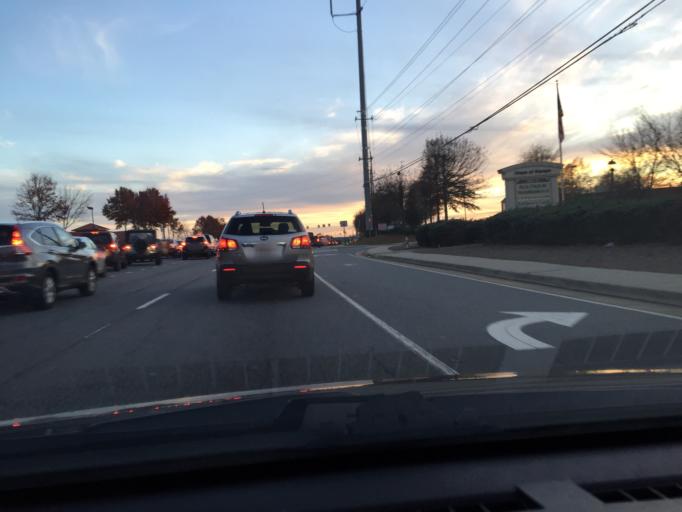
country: US
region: Georgia
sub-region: Fulton County
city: Johns Creek
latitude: 34.0205
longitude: -84.1895
